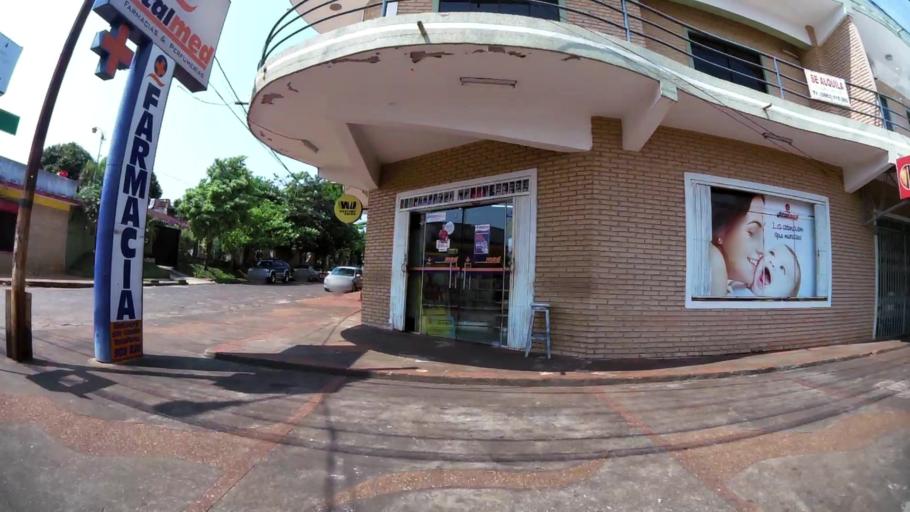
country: PY
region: Alto Parana
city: Presidente Franco
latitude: -25.5251
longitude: -54.6190
